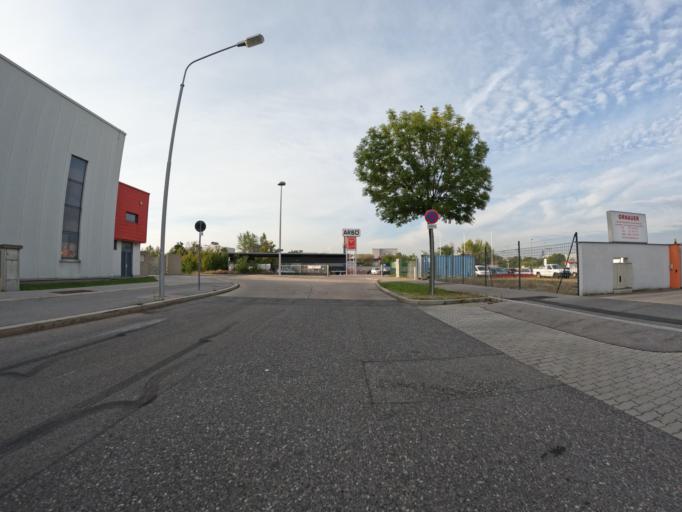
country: AT
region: Lower Austria
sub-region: Politischer Bezirk Wien-Umgebung
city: Gerasdorf bei Wien
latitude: 48.2554
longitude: 16.4676
